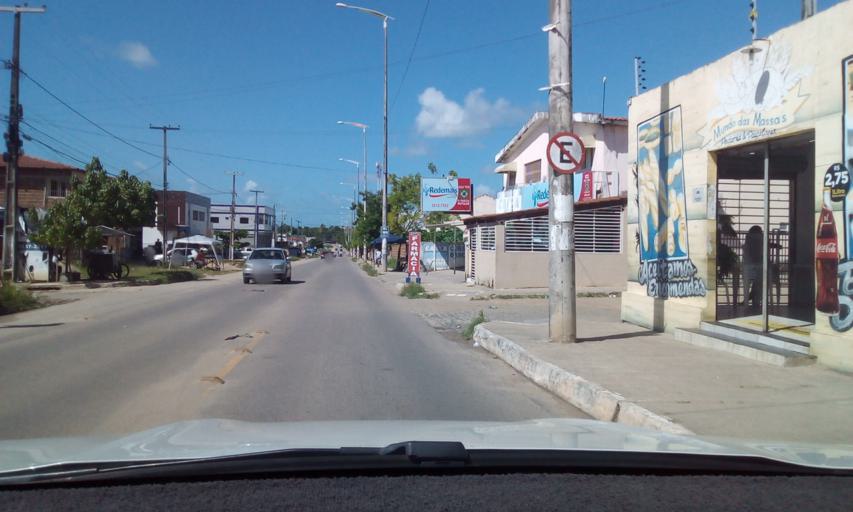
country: BR
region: Paraiba
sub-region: Joao Pessoa
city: Joao Pessoa
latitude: -7.2014
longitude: -34.8332
